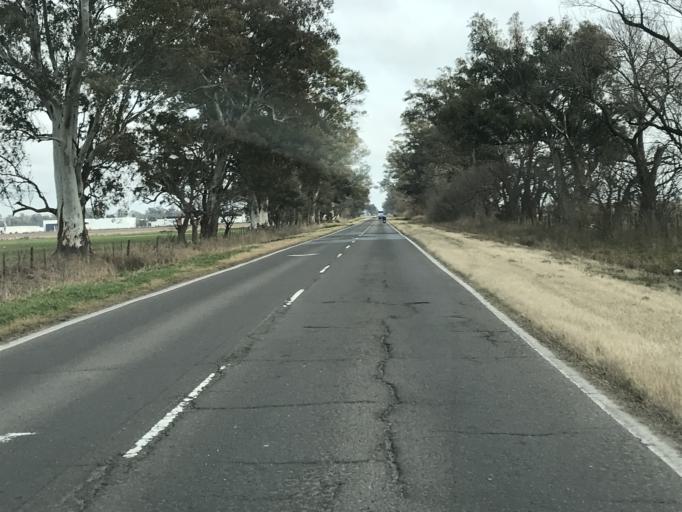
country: AR
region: Santa Fe
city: Canada de Gomez
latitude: -32.8223
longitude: -61.3247
